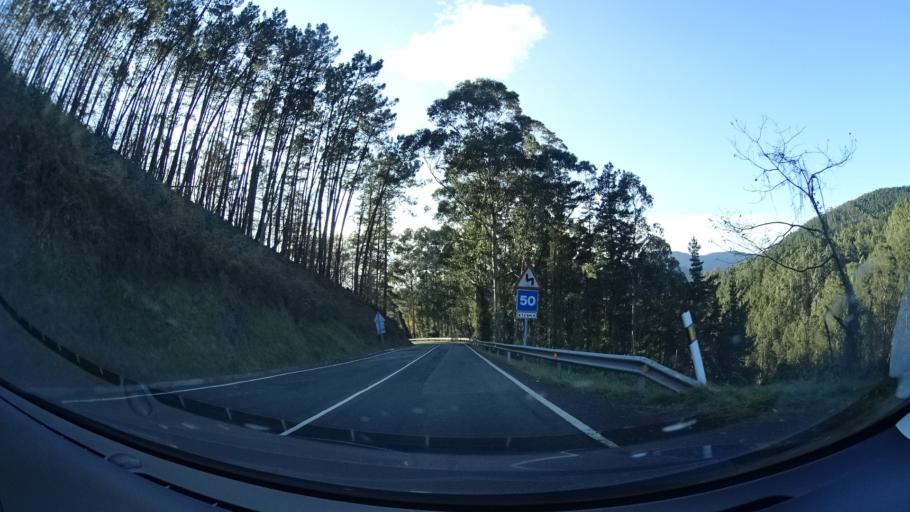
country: ES
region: Basque Country
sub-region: Bizkaia
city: Bakio
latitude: 43.3858
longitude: -2.7851
